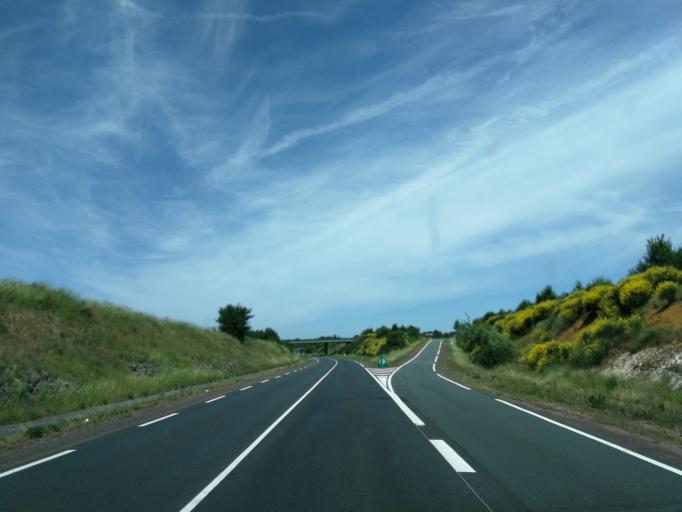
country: FR
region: Pays de la Loire
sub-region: Departement de la Vendee
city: Pissotte
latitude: 46.5001
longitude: -0.8231
